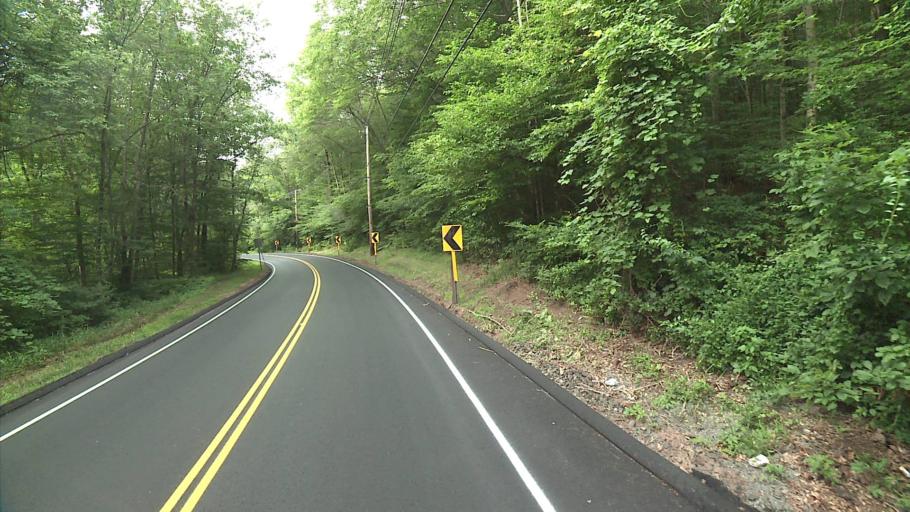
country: US
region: Connecticut
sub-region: New Haven County
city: Wallingford Center
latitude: 41.4171
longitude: -72.8011
